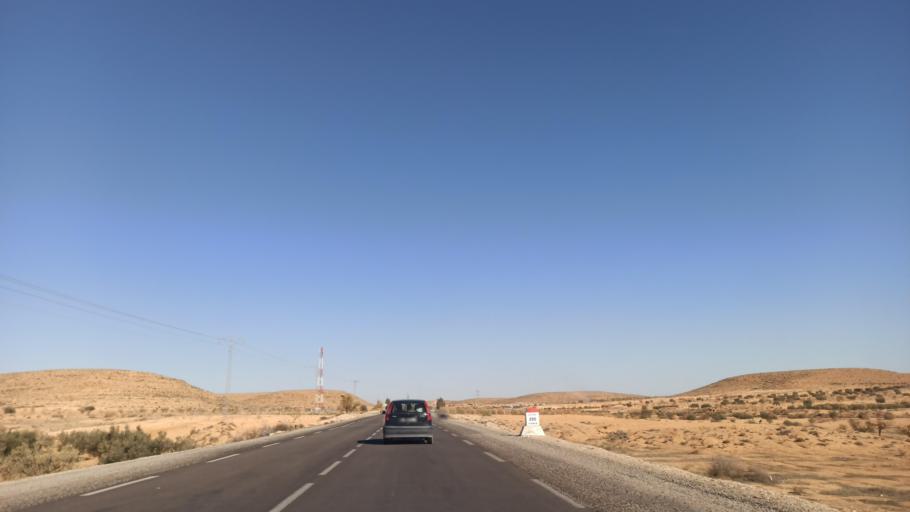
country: TN
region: Sidi Bu Zayd
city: Bi'r al Hufayy
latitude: 34.7131
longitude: 9.0523
